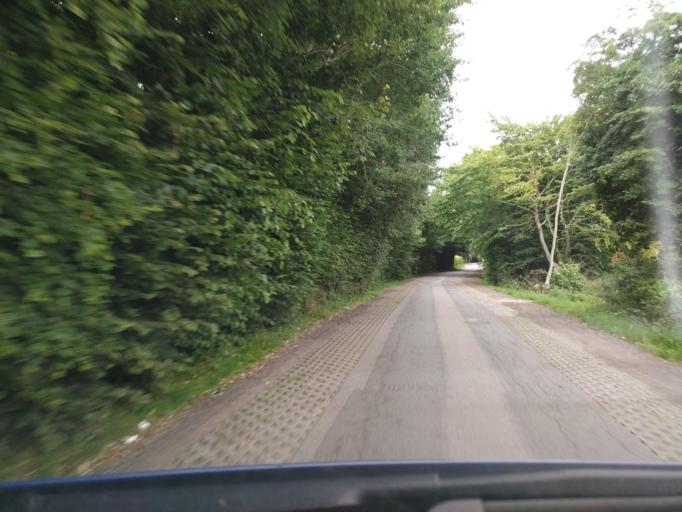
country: DE
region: Schleswig-Holstein
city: Schuby
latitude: 54.5117
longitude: 9.5125
